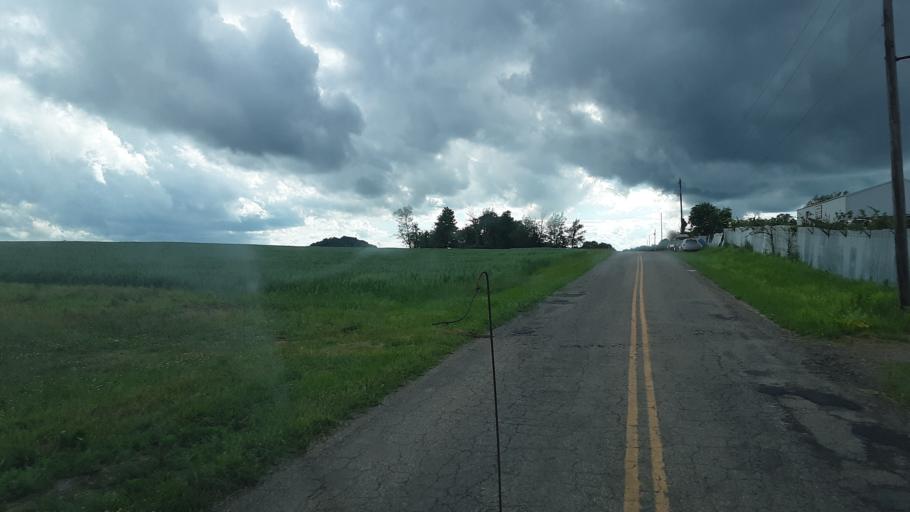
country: US
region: Ohio
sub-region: Carroll County
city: Carrollton
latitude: 40.5601
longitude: -81.0715
